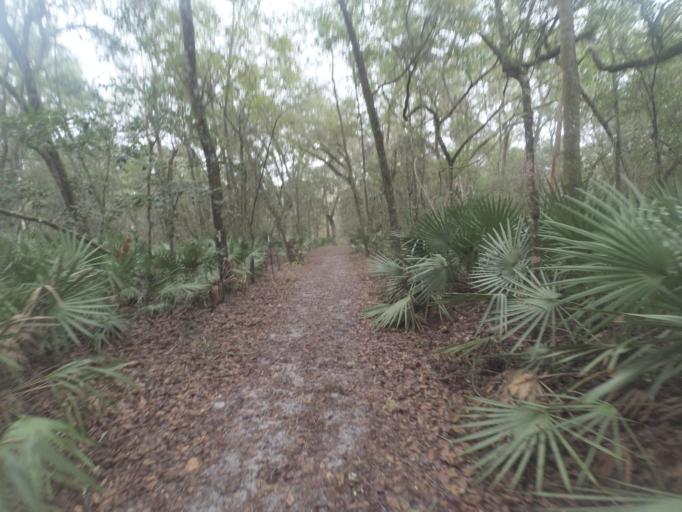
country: US
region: Florida
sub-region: Alachua County
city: Gainesville
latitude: 29.5391
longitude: -82.2890
